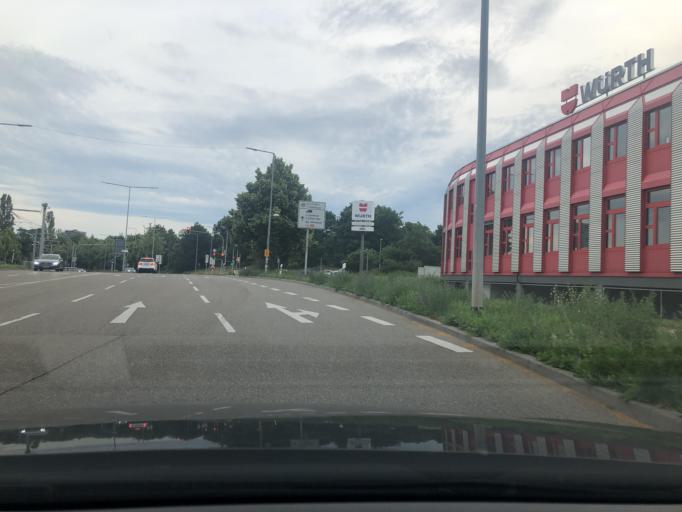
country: DE
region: Baden-Wuerttemberg
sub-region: Regierungsbezirk Stuttgart
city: Stuttgart Muehlhausen
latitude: 48.8186
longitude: 9.2045
